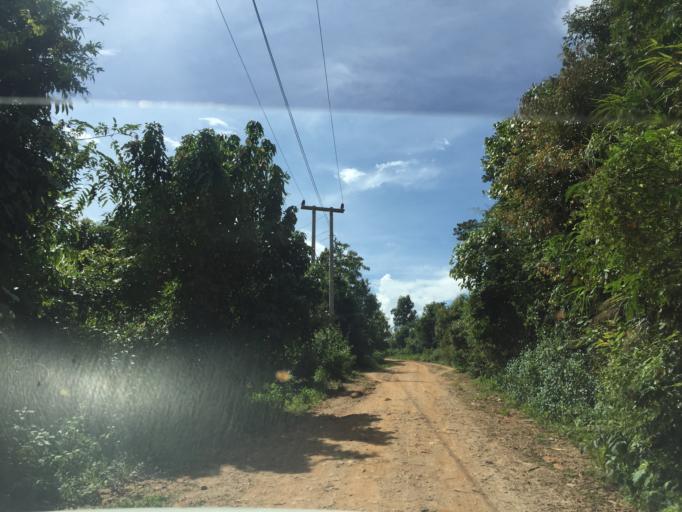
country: LA
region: Xiangkhoang
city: Muang Phonsavan
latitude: 19.3381
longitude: 103.5049
